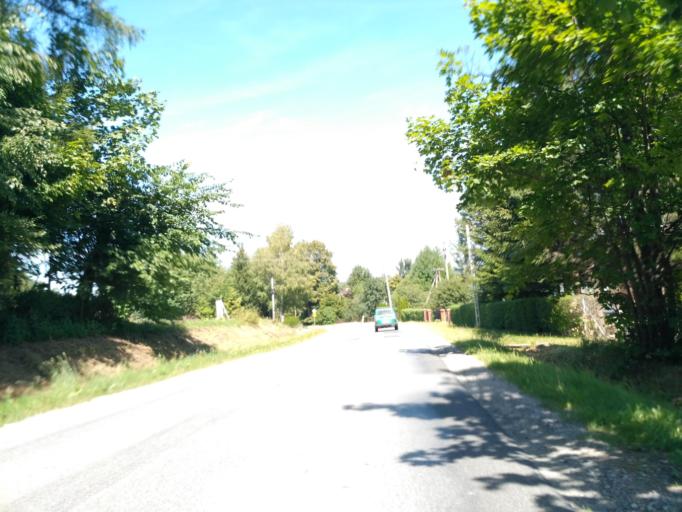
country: PL
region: Subcarpathian Voivodeship
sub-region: Powiat sanocki
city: Nowosielce-Gniewosz
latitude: 49.5244
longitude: 22.1041
